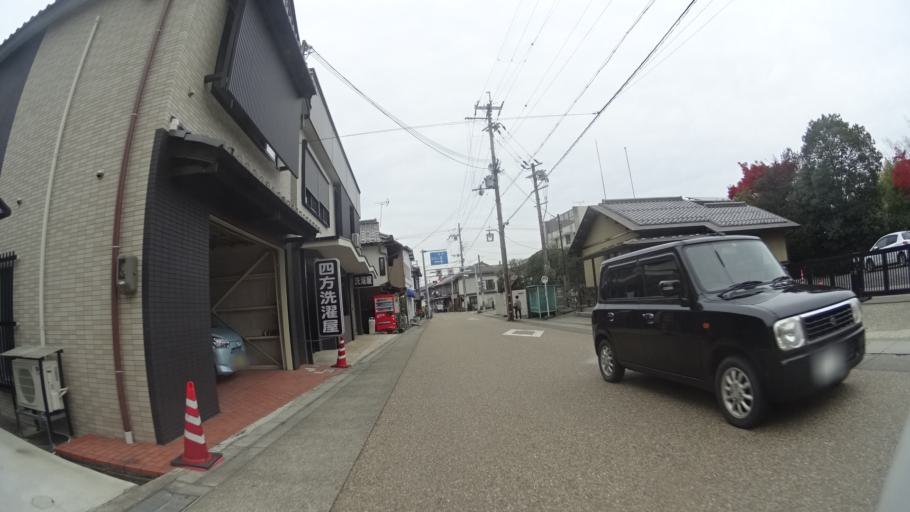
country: JP
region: Kyoto
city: Ayabe
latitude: 35.2968
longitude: 135.2603
